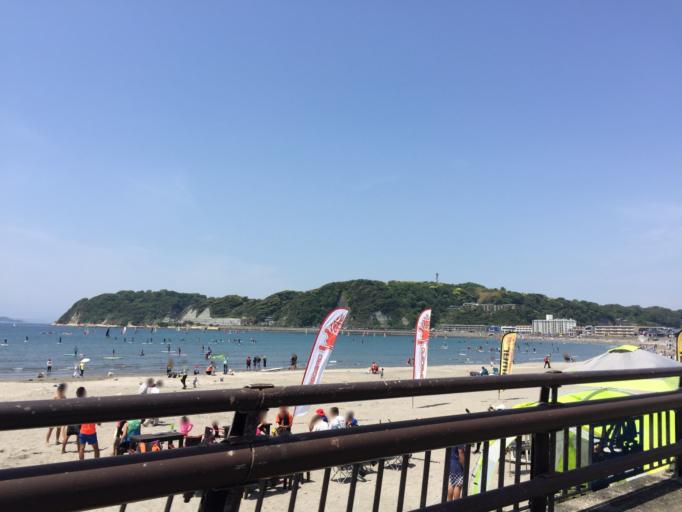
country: JP
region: Kanagawa
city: Zushi
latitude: 35.2890
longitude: 139.5740
